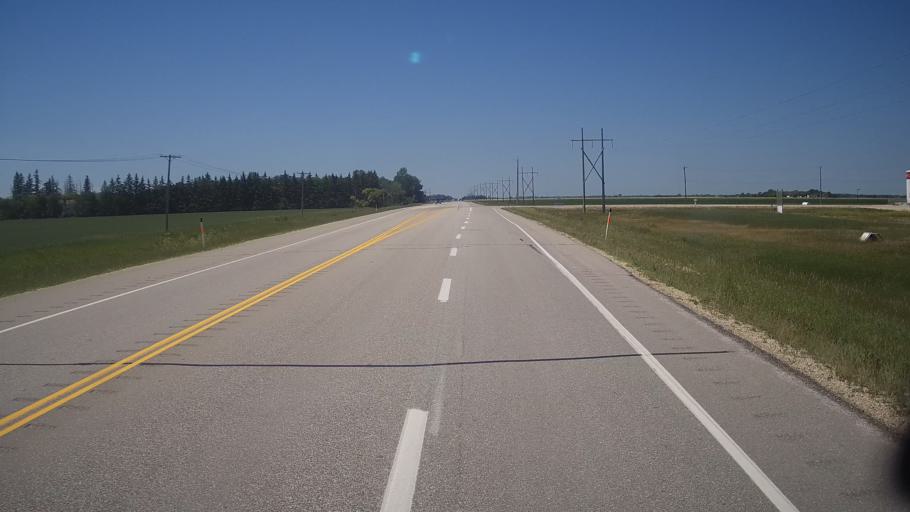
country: CA
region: Manitoba
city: Stonewall
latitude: 50.1231
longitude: -97.5416
